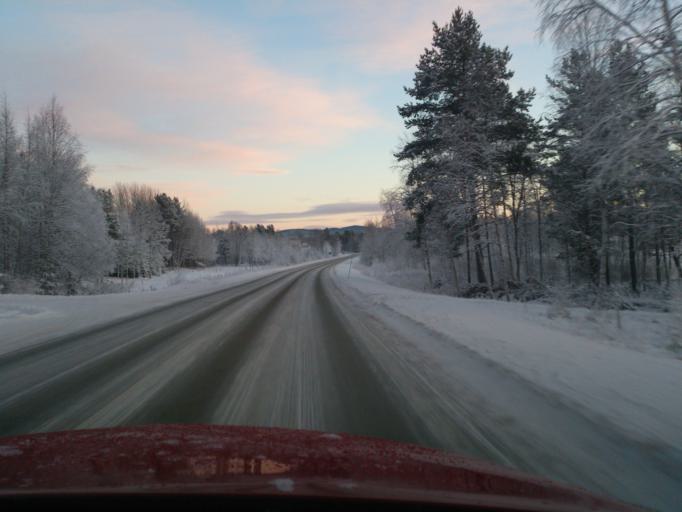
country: SE
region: Jaemtland
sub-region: Harjedalens Kommun
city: Sveg
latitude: 62.4112
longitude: 13.6808
